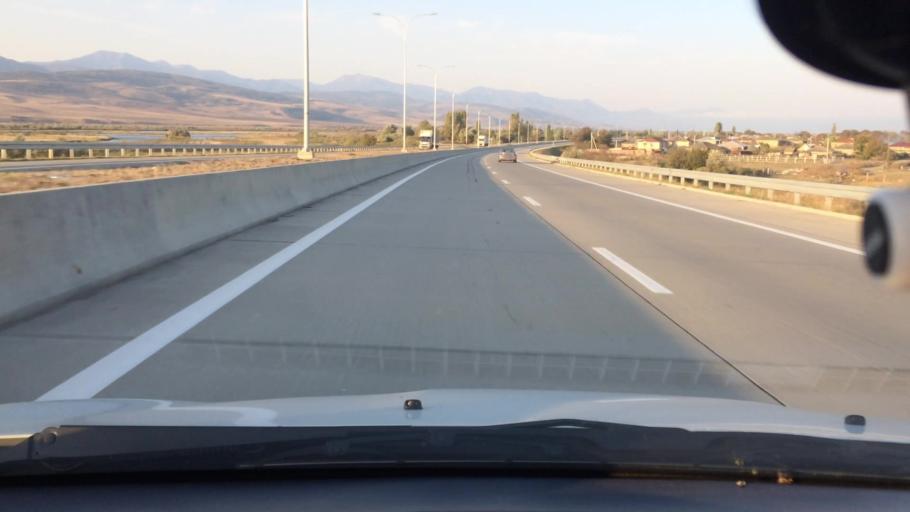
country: GE
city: Agara
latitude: 42.0318
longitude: 43.8423
